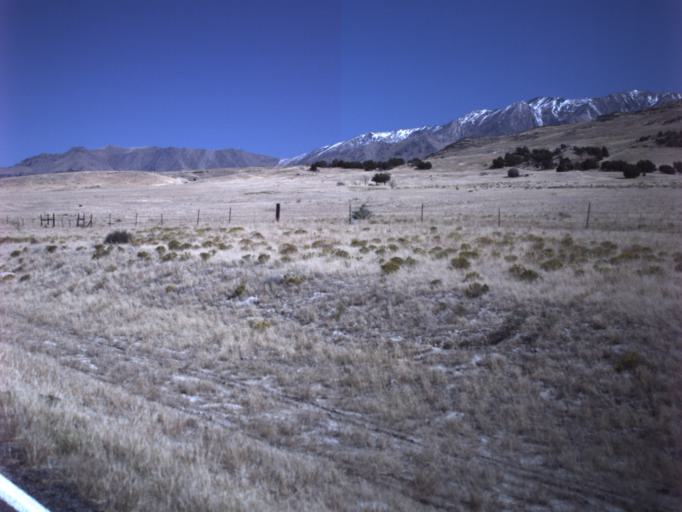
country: US
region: Utah
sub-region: Tooele County
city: Grantsville
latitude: 40.5724
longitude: -112.7296
